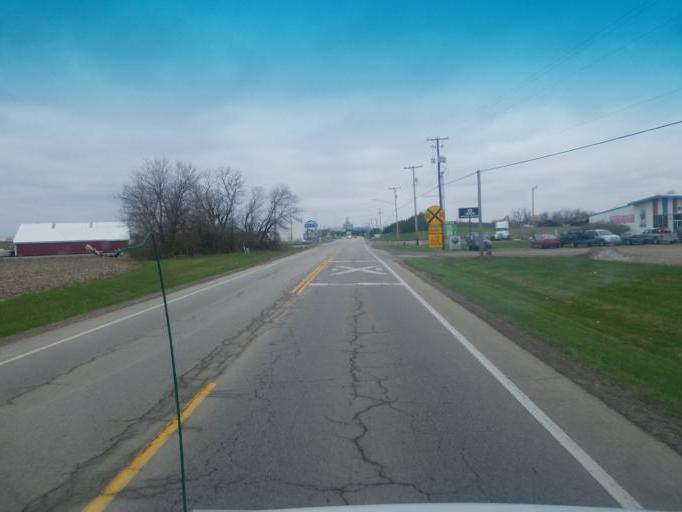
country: US
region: Ohio
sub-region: Van Wert County
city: Van Wert
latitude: 40.8928
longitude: -84.5801
